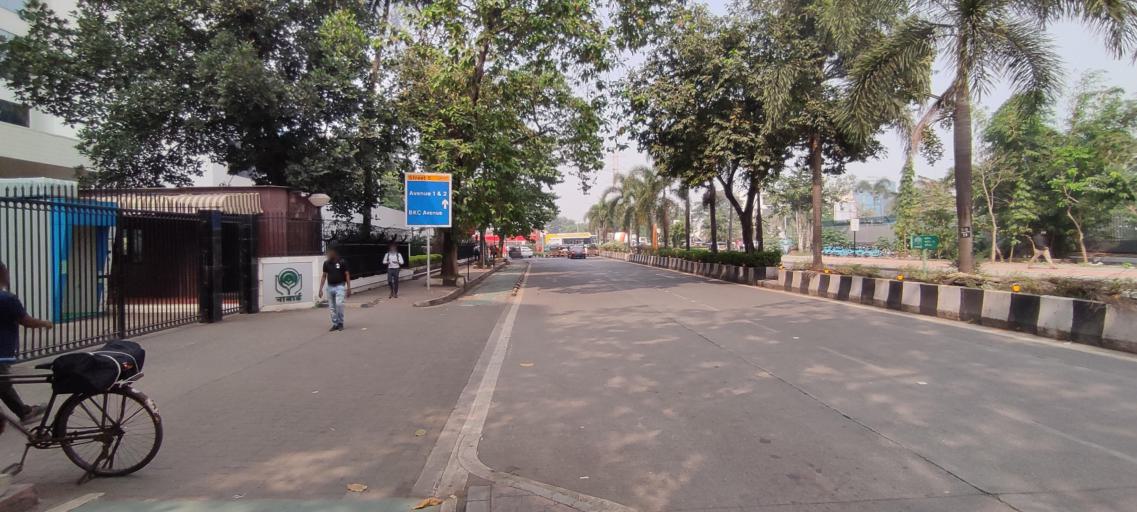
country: IN
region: Maharashtra
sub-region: Mumbai Suburban
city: Mumbai
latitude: 19.0645
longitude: 72.8629
